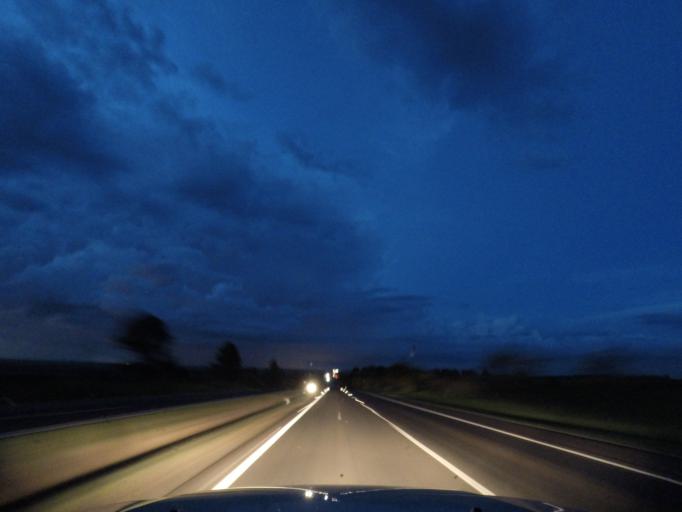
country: BR
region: Minas Gerais
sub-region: Uberlandia
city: Uberlandia
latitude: -19.2357
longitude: -48.1412
